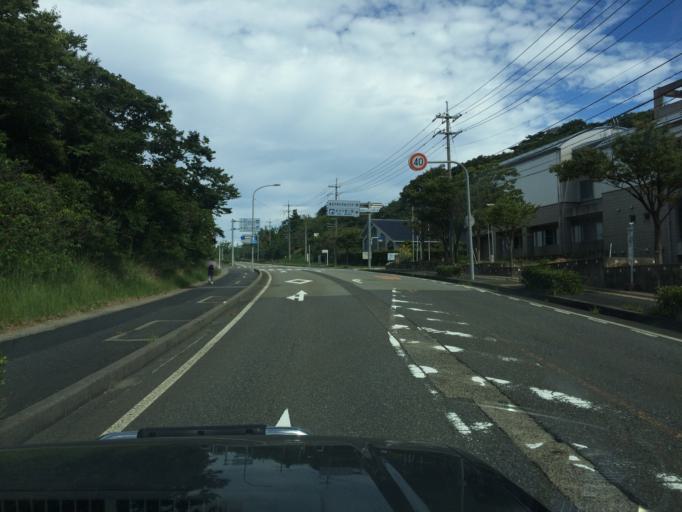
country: JP
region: Tottori
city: Kurayoshi
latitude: 35.5199
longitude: 134.0005
